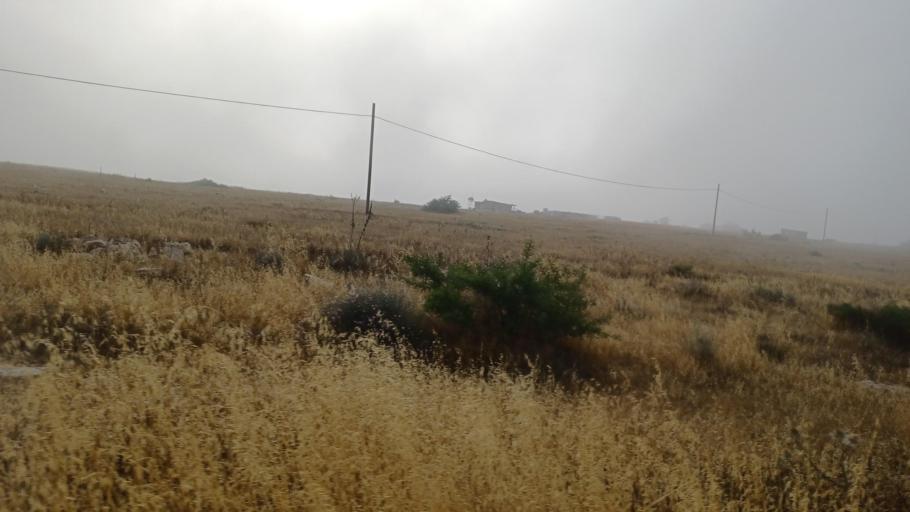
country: CY
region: Ammochostos
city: Acheritou
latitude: 35.0990
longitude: 33.8774
